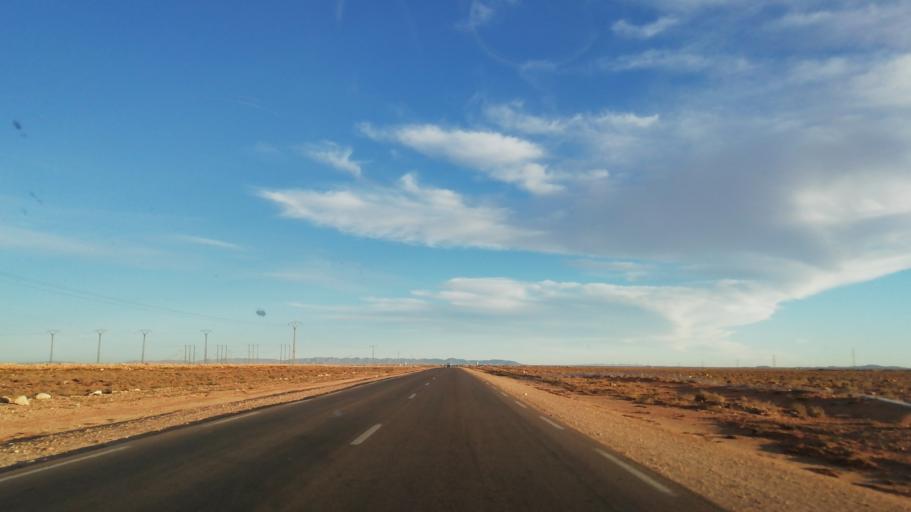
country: DZ
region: Wilaya de Naama
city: Naama
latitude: 33.7364
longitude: -0.7640
